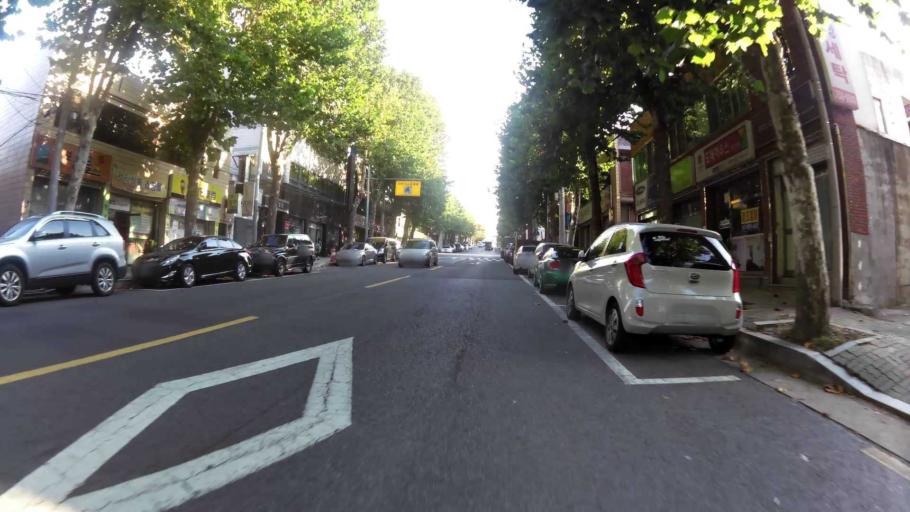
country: KR
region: Daegu
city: Daegu
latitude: 35.8641
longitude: 128.6393
